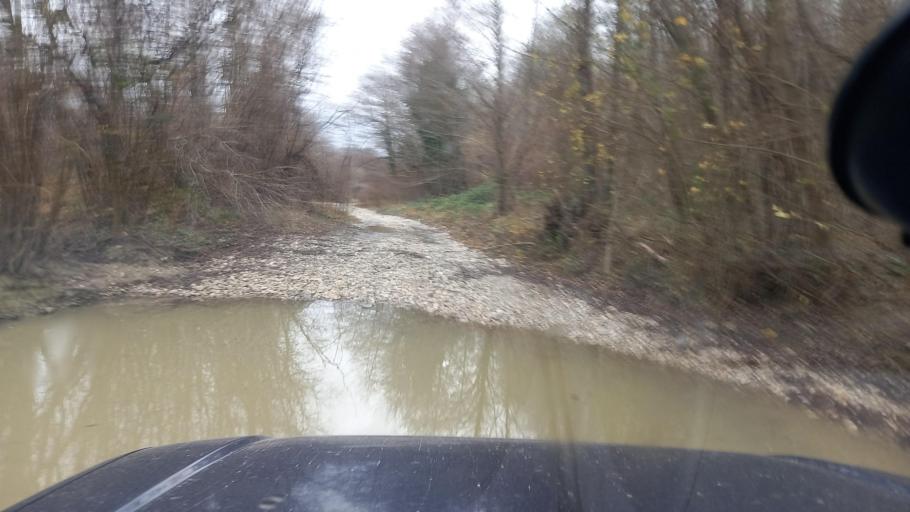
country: RU
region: Krasnodarskiy
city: Pshada
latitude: 44.4936
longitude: 38.4207
